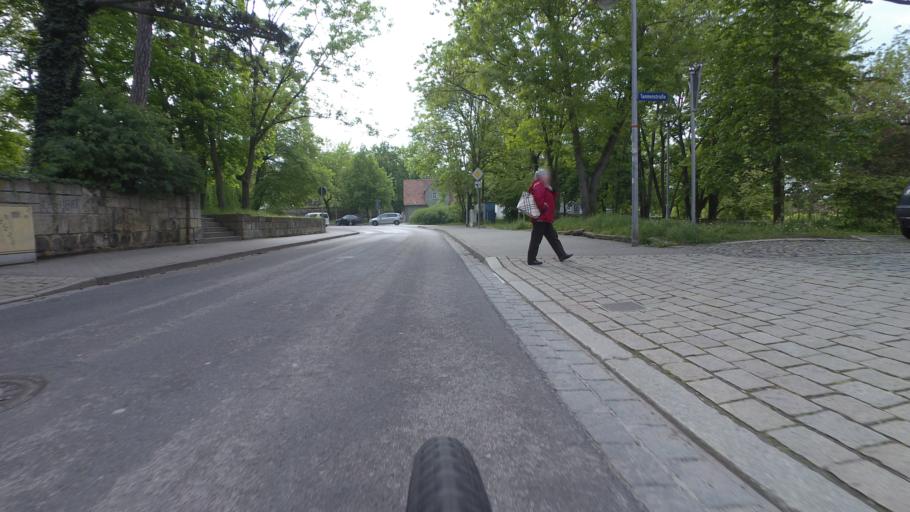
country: DE
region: Saxony-Anhalt
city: Halberstadt
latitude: 51.8944
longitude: 11.0409
